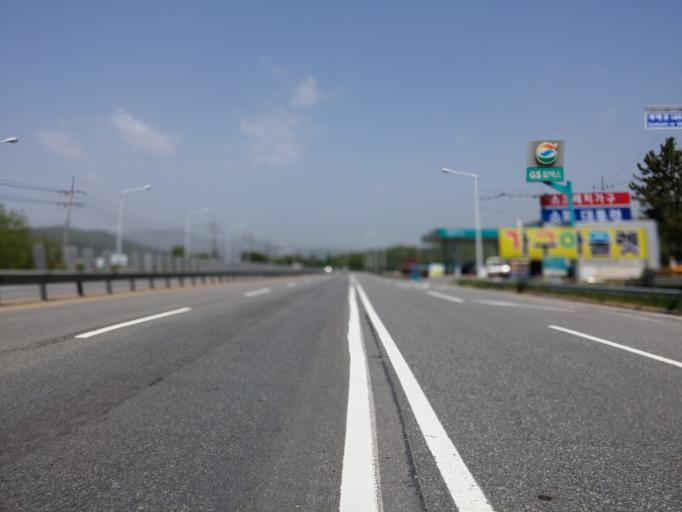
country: KR
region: Daejeon
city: Daejeon
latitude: 36.2738
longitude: 127.2682
